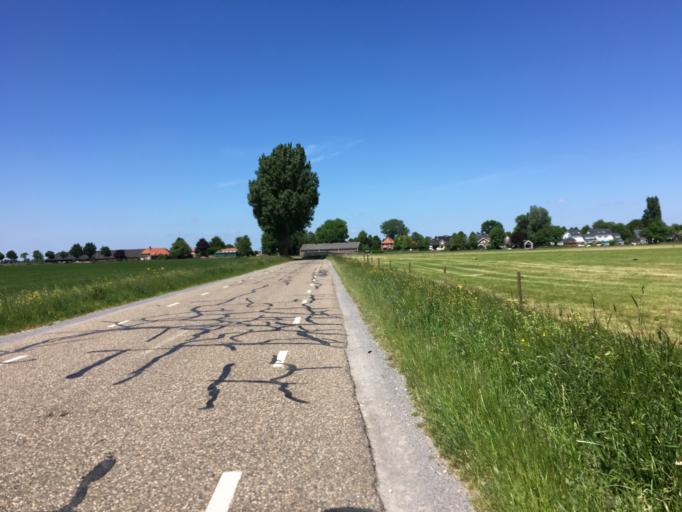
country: NL
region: Gelderland
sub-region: Gemeente Maasdriel
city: Hedel
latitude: 51.7332
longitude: 5.2311
